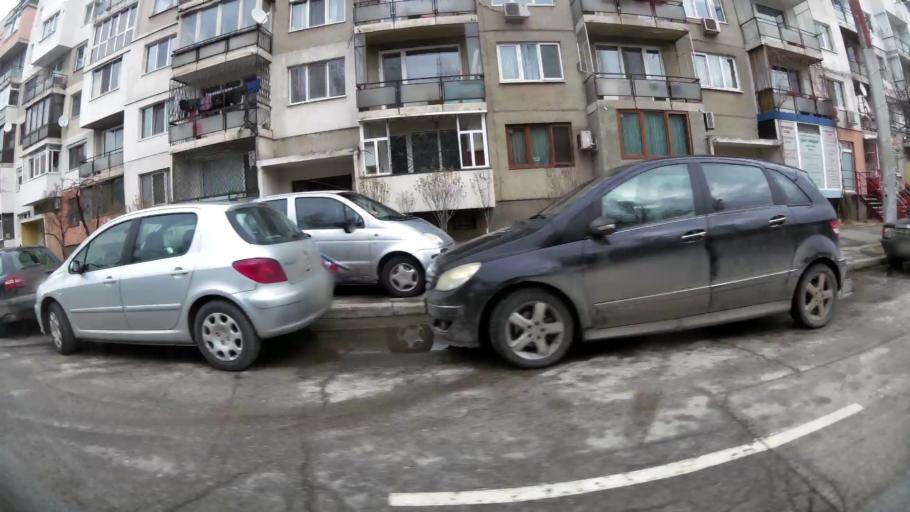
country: BG
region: Sofiya
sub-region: Obshtina Bozhurishte
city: Bozhurishte
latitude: 42.7270
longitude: 23.2523
